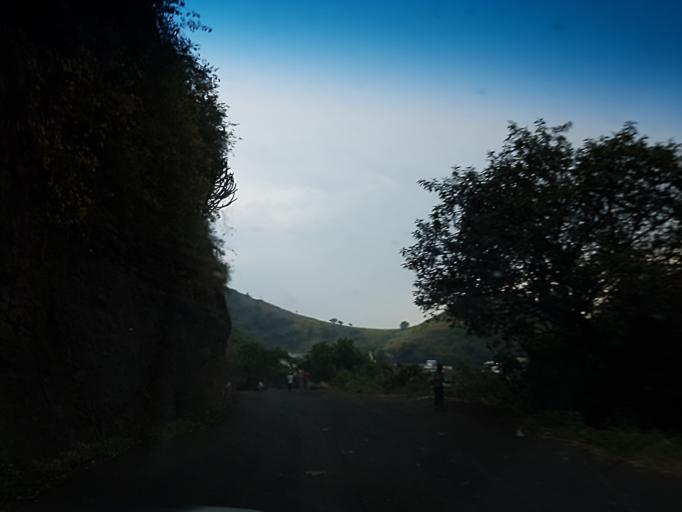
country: CD
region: Nord Kivu
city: Goma
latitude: -1.6815
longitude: 29.2224
